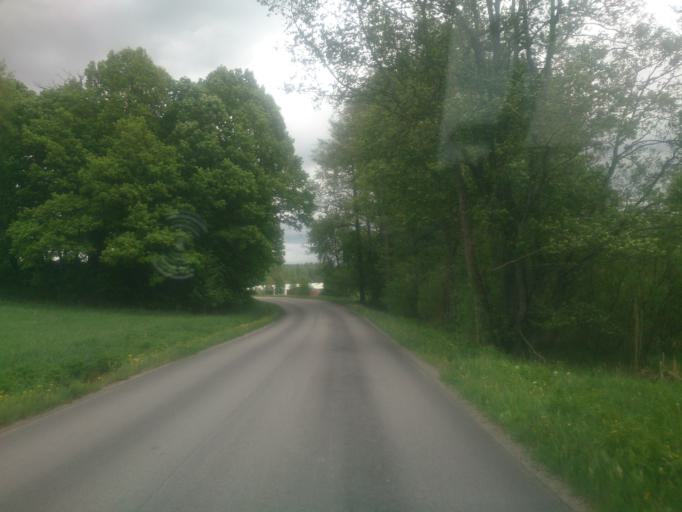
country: SE
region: OEstergoetland
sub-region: Atvidabergs Kommun
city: Atvidaberg
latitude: 58.2184
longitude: 16.0411
